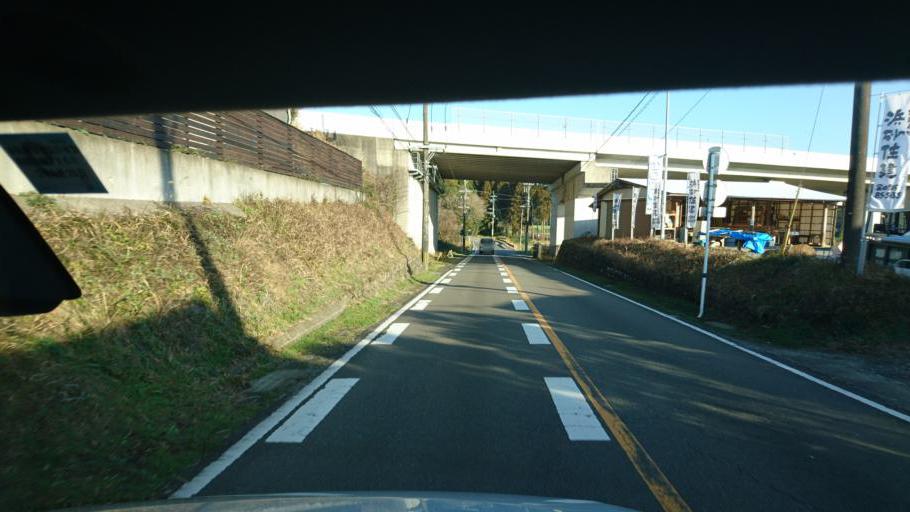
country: JP
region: Miyazaki
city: Miyazaki-shi
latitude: 31.8549
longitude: 131.3737
